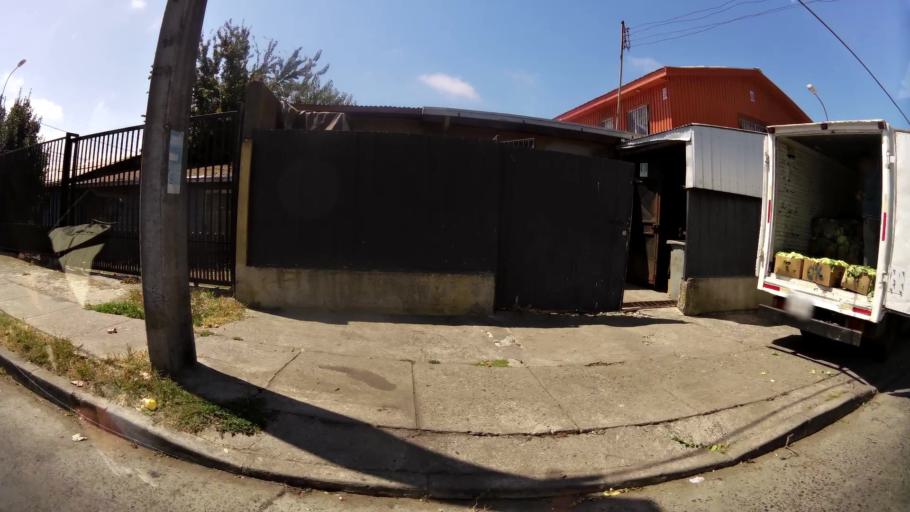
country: CL
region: Biobio
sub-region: Provincia de Concepcion
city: Concepcion
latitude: -36.8075
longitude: -73.0435
